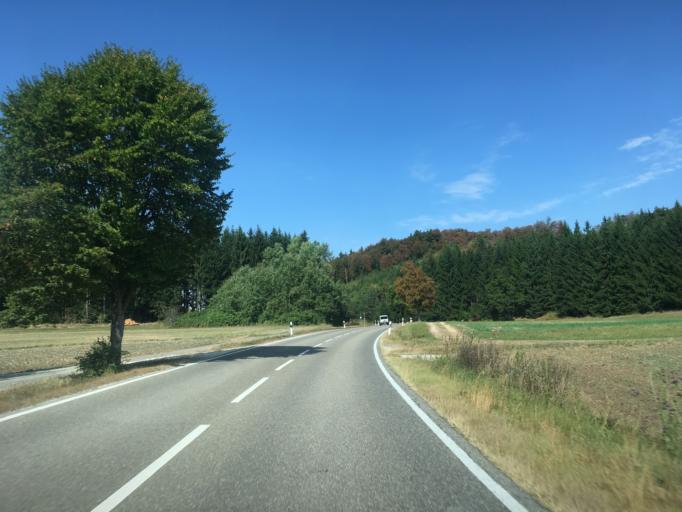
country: DE
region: Baden-Wuerttemberg
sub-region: Tuebingen Region
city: Trochtelfingen
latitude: 48.3728
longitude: 9.1982
